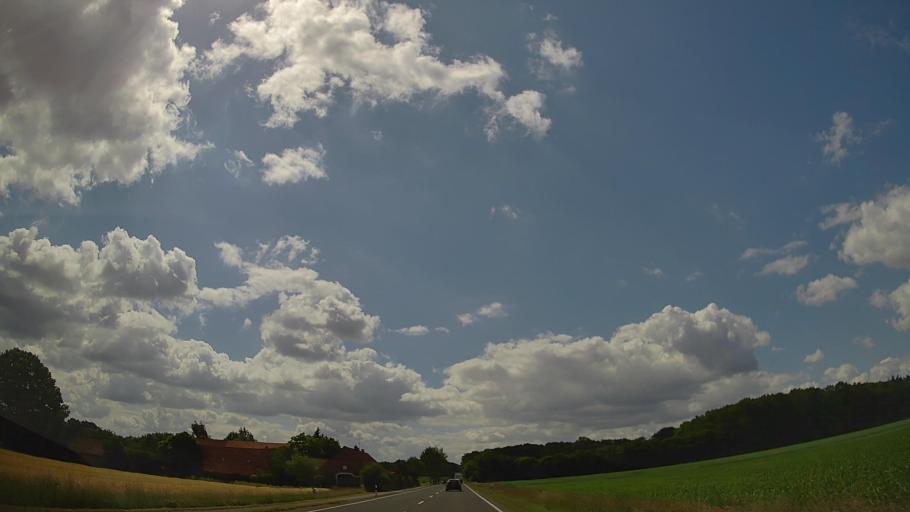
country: DE
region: Lower Saxony
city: Diepholz
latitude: 52.6650
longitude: 8.3296
